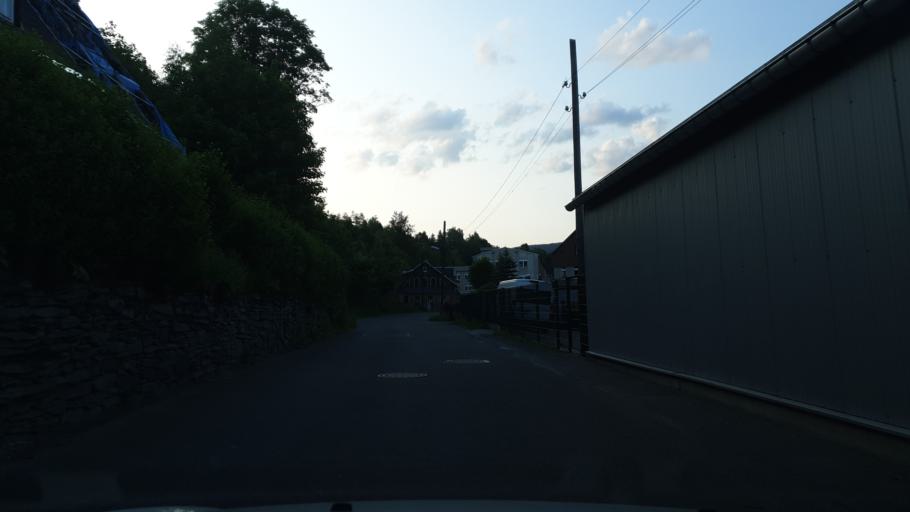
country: DE
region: Saxony
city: Klingenthal
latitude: 50.3640
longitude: 12.4678
